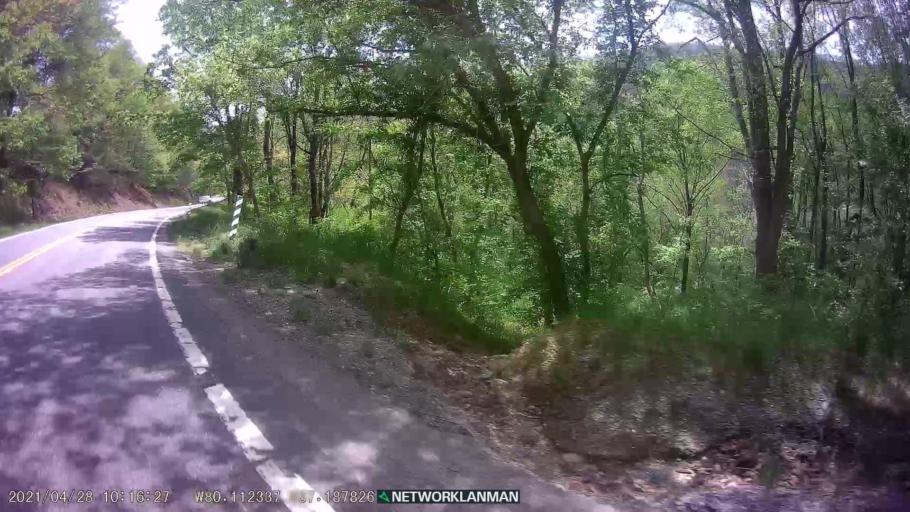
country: US
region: Virginia
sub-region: Roanoke County
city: Cave Spring
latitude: 37.1878
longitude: -80.1121
